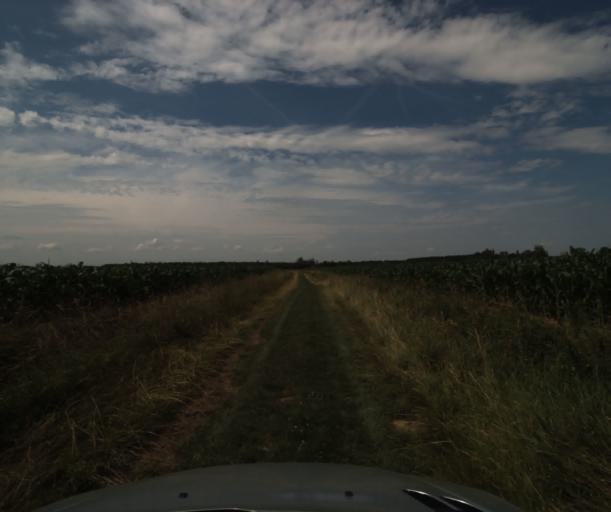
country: FR
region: Midi-Pyrenees
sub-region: Departement de la Haute-Garonne
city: Labastidette
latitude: 43.4817
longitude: 1.2222
